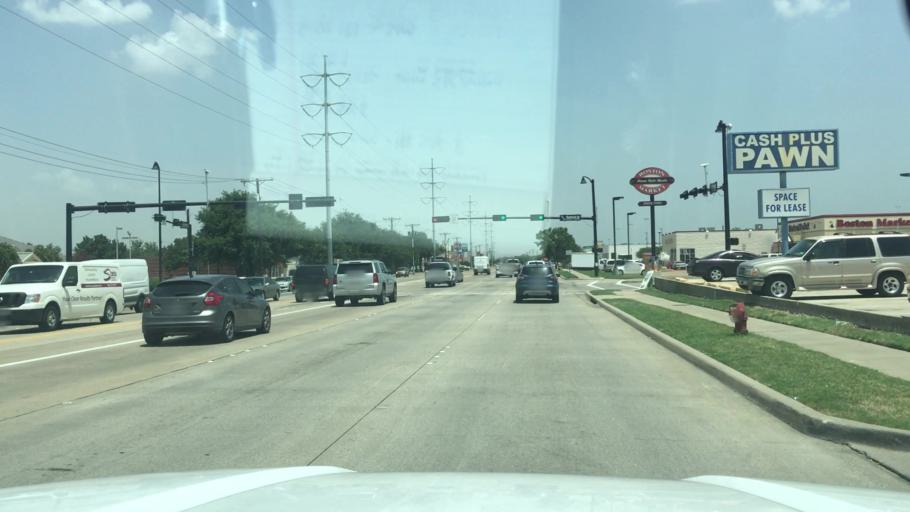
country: US
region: Texas
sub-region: Tarrant County
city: Watauga
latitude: 32.8549
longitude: -97.2383
